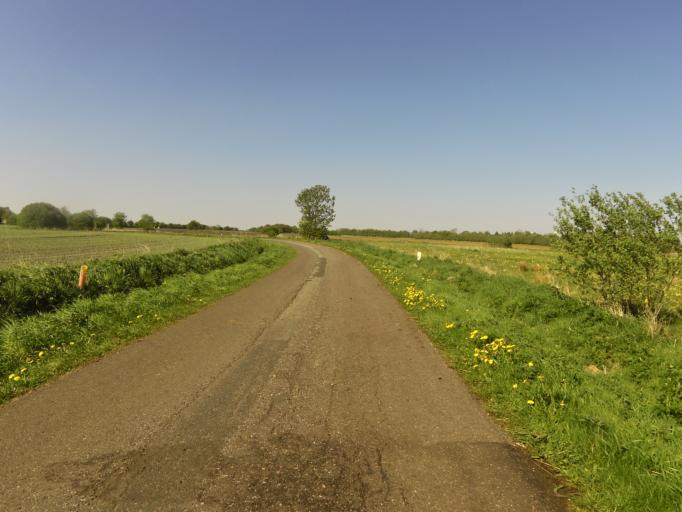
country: DK
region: South Denmark
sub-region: Tonder Kommune
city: Sherrebek
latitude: 55.2104
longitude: 8.8435
